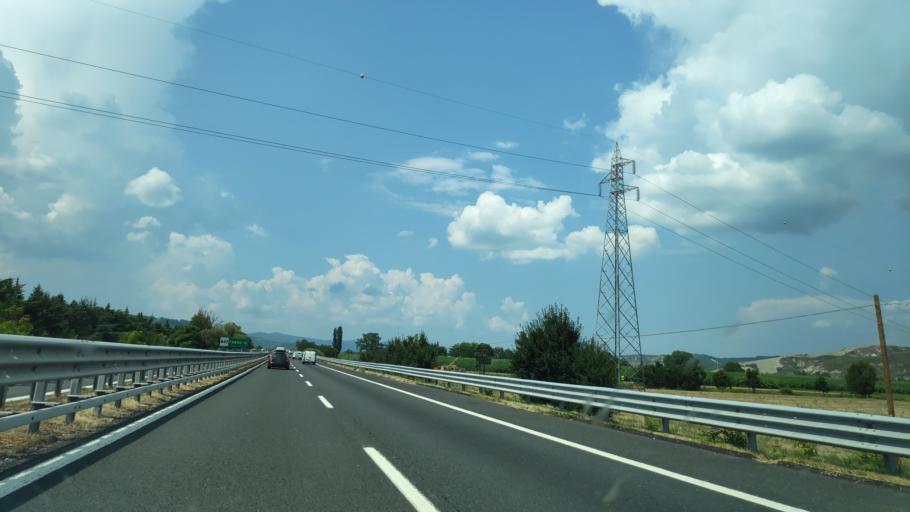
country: IT
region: Umbria
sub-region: Provincia di Terni
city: Sferracavallo
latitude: 42.7346
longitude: 12.1067
